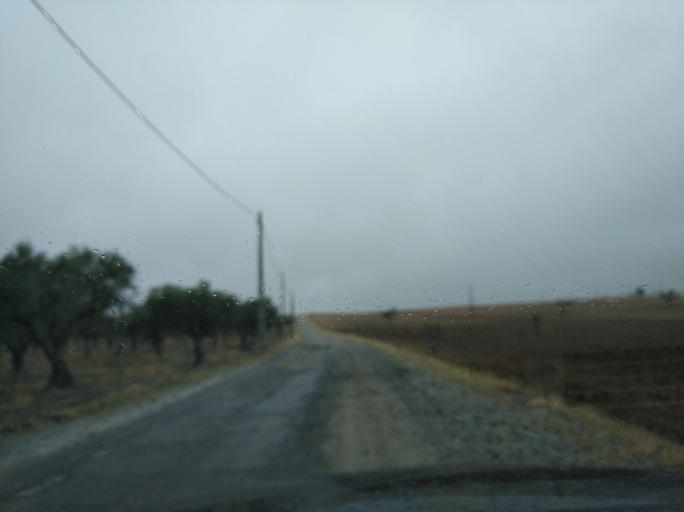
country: PT
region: Portalegre
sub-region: Campo Maior
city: Campo Maior
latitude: 38.9782
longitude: -7.0896
